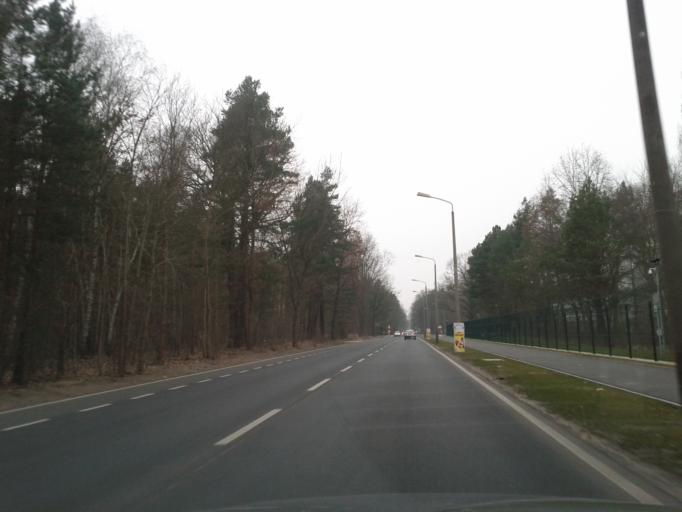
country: DE
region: Berlin
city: Adlershof
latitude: 52.4482
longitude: 13.5518
